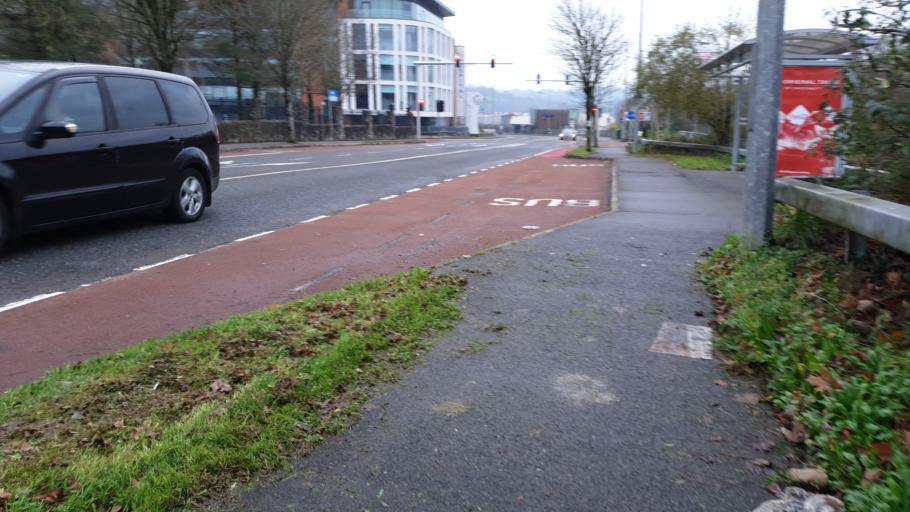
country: IE
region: Munster
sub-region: County Cork
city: Cork
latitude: 51.8868
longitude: -8.4075
